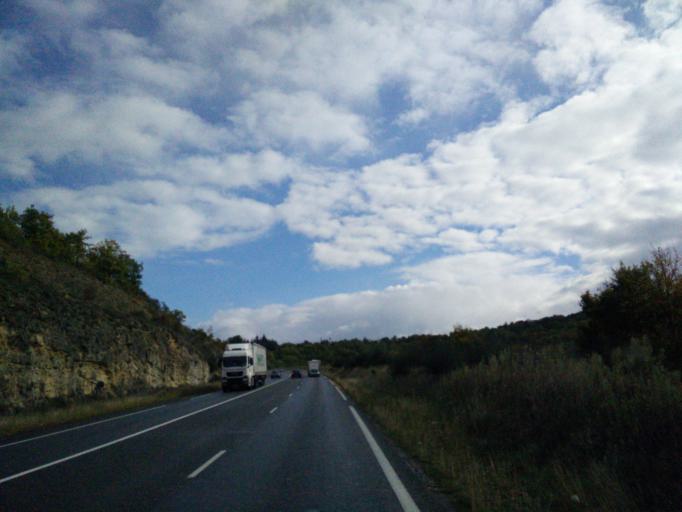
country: FR
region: Midi-Pyrenees
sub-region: Departement du Lot
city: Cahors
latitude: 44.4504
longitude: 1.4136
